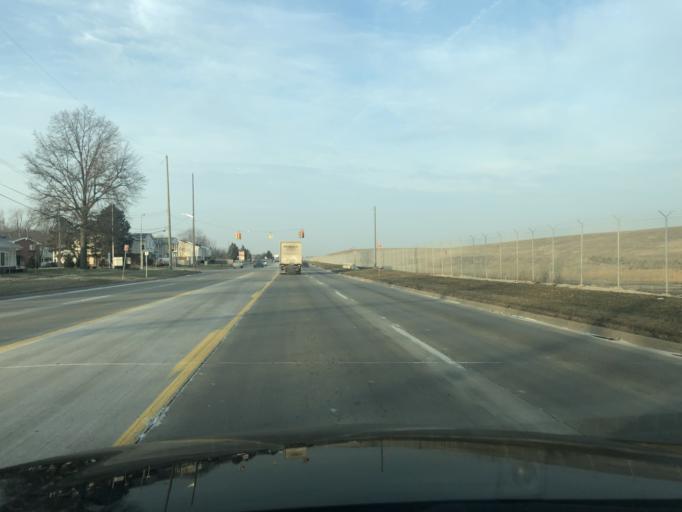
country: US
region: Michigan
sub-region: Wayne County
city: Romulus
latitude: 42.1954
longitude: -83.3353
